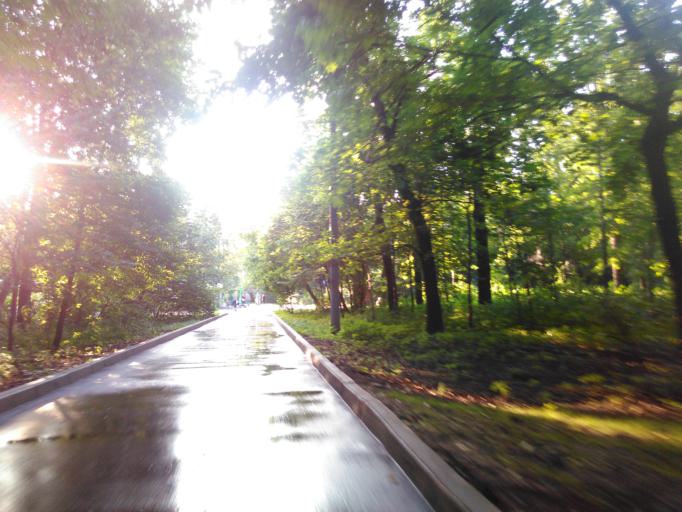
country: RU
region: Moscow
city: Sokol'niki
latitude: 55.7926
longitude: 37.6695
